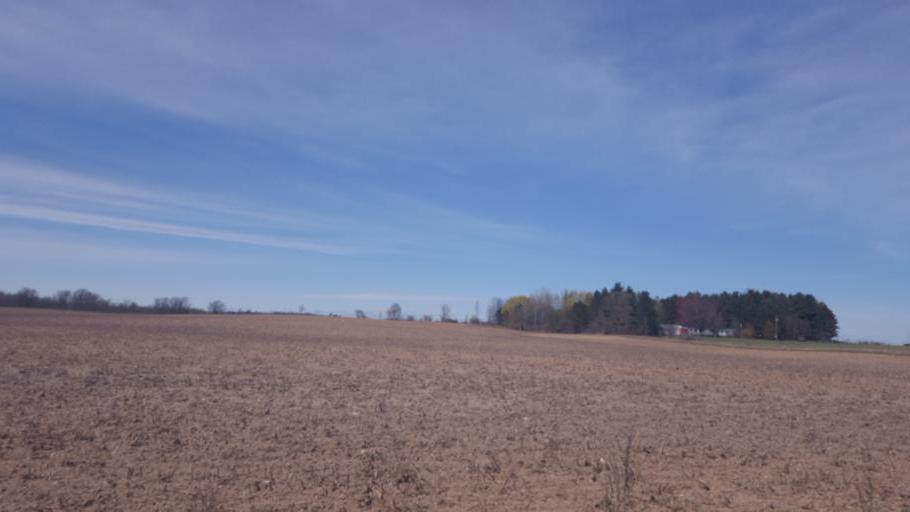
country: US
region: Michigan
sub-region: Gladwin County
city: Gladwin
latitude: 44.0599
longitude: -84.4789
